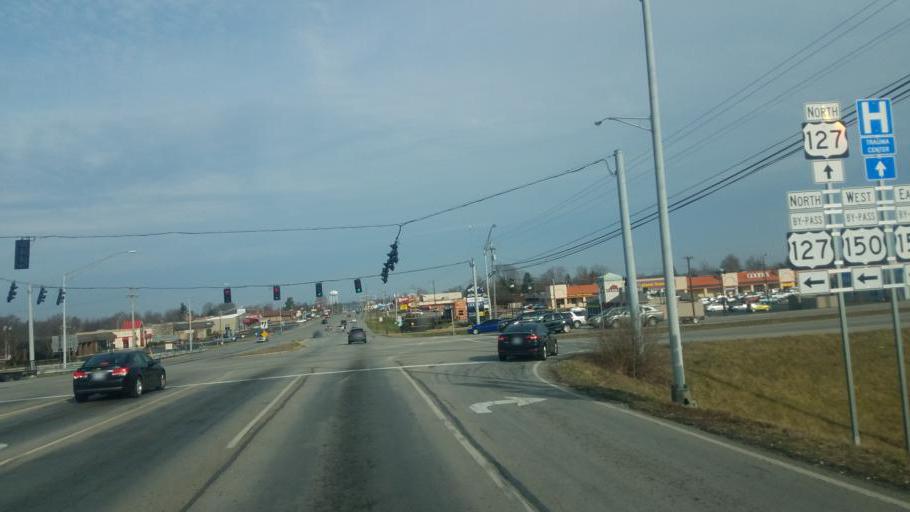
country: US
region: Kentucky
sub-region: Boyle County
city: Danville
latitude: 37.6170
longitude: -84.7745
